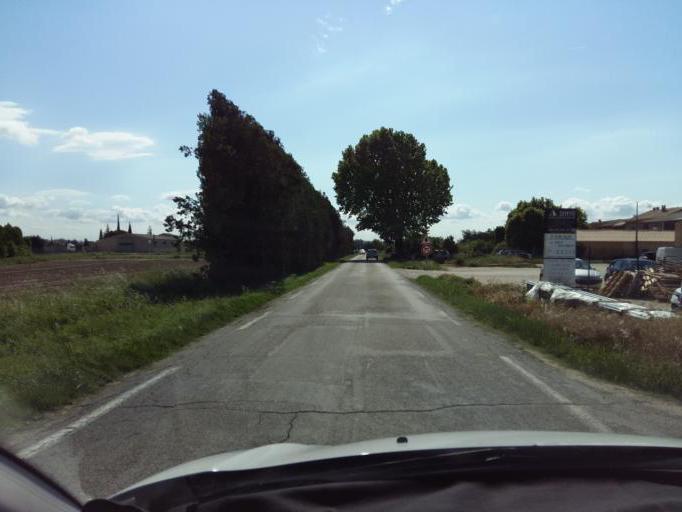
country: FR
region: Provence-Alpes-Cote d'Azur
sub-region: Departement du Vaucluse
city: Robion
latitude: 43.8681
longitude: 5.1224
